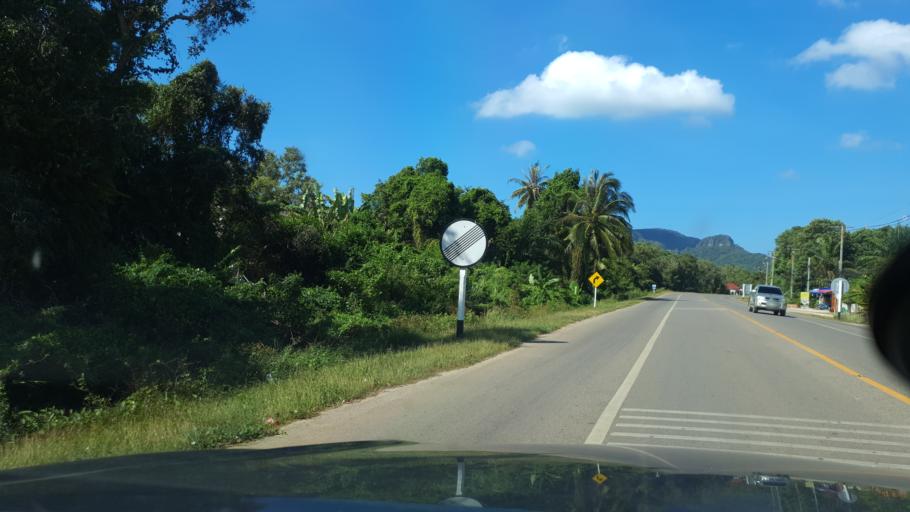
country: TH
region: Krabi
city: Krabi
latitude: 8.0267
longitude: 98.8773
